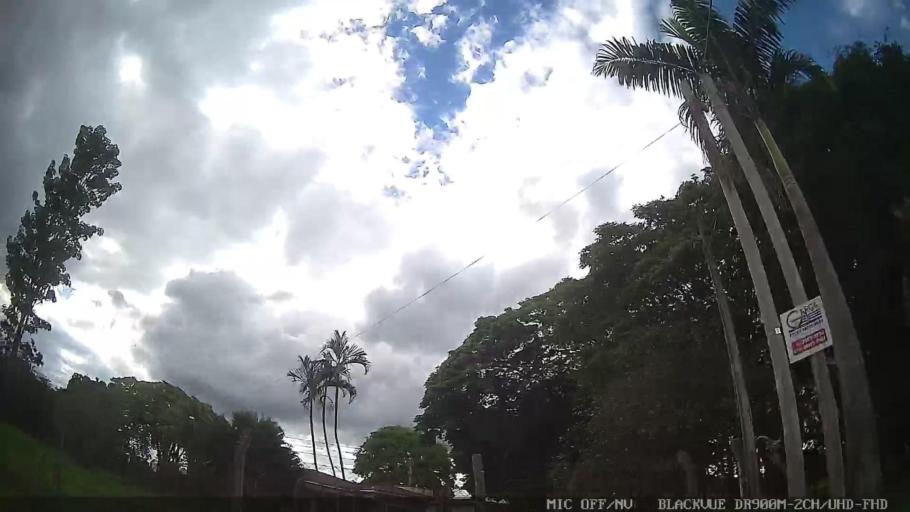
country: BR
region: Sao Paulo
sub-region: Jaguariuna
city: Jaguariuna
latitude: -22.6695
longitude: -47.0685
